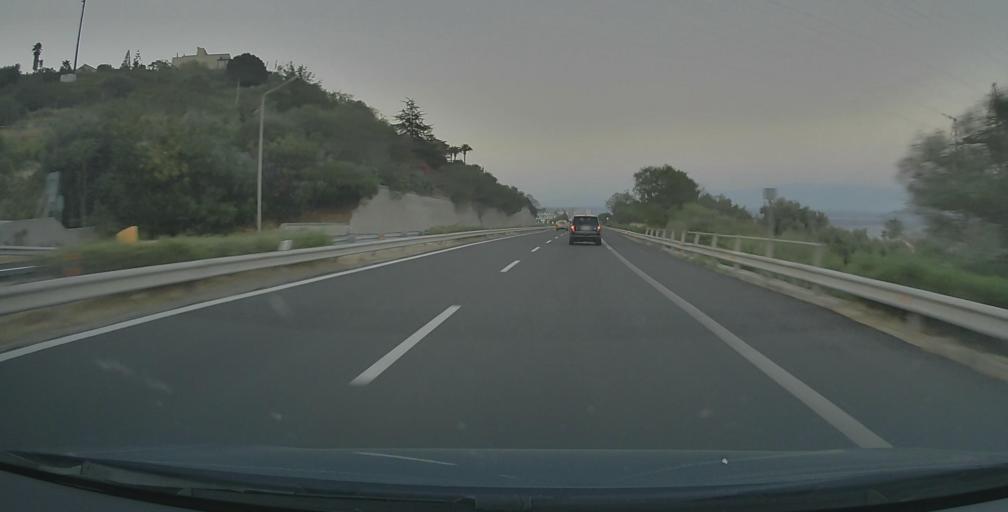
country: IT
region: Sicily
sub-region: Messina
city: Roccalumera
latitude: 37.9766
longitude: 15.3935
